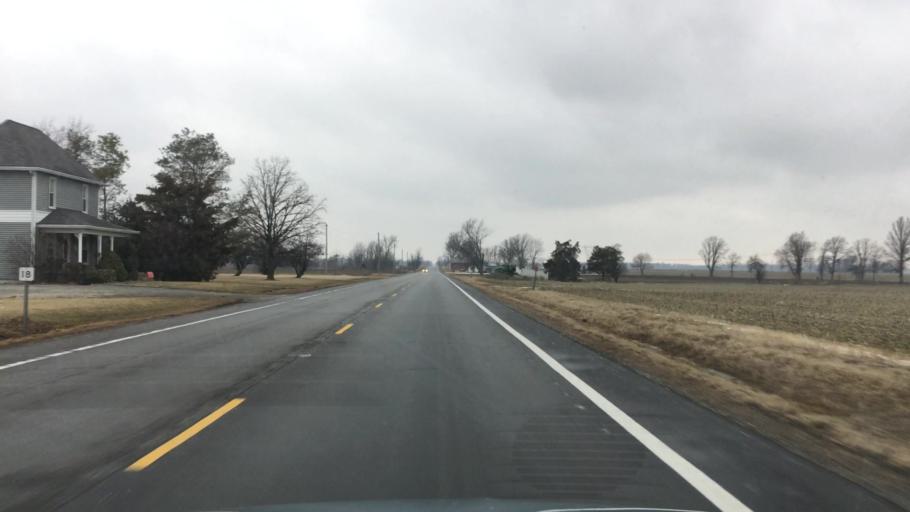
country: US
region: Ohio
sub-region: Auglaize County
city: Saint Marys
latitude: 40.5864
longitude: -84.4638
